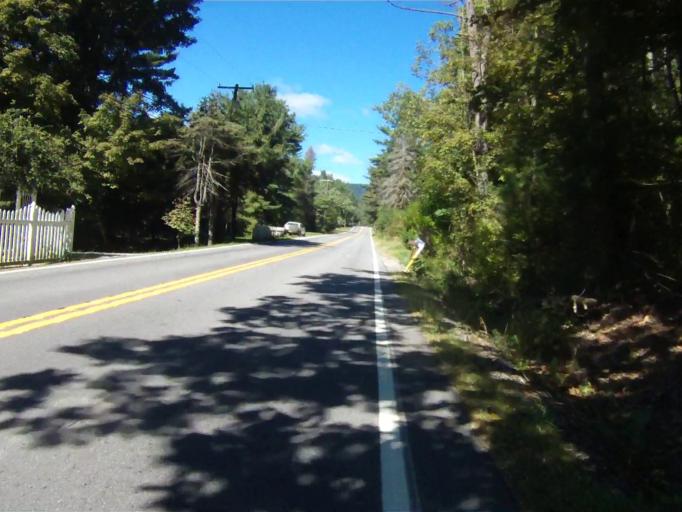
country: US
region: Pennsylvania
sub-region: Centre County
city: Milesburg
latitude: 40.9176
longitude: -77.8916
